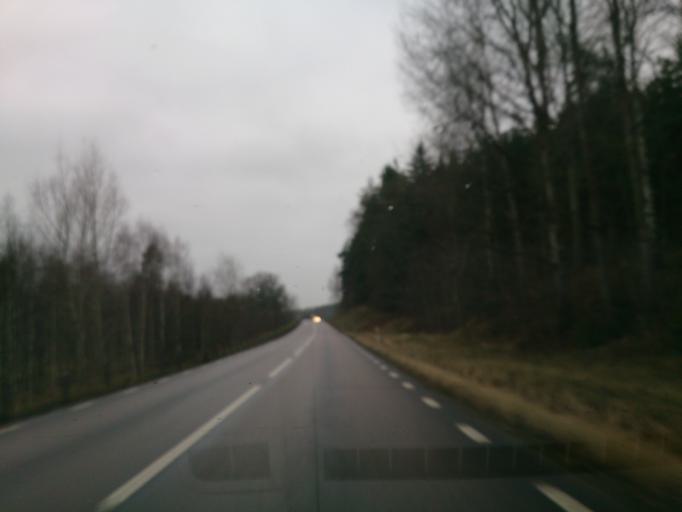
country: SE
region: OEstergoetland
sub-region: Atvidabergs Kommun
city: Atvidaberg
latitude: 58.2790
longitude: 15.9078
